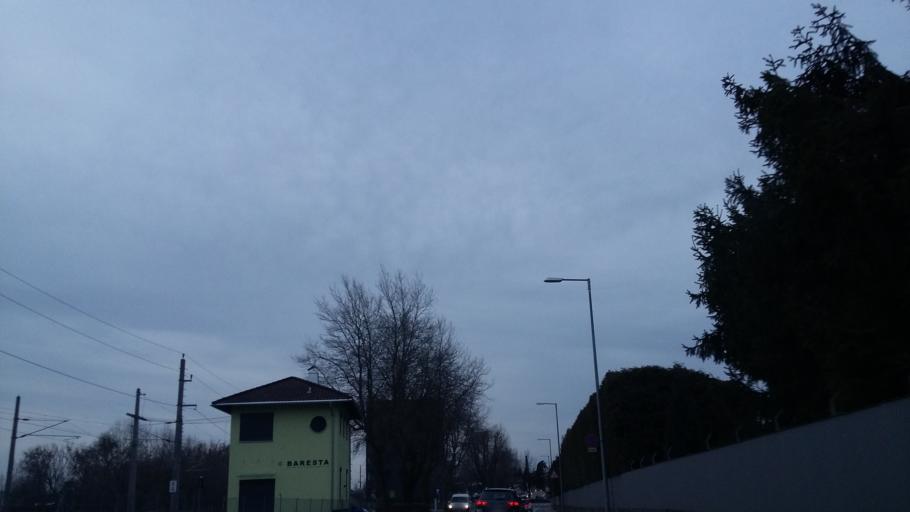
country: AT
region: Vorarlberg
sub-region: Politischer Bezirk Bregenz
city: Lochau
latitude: 47.5281
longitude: 9.7444
